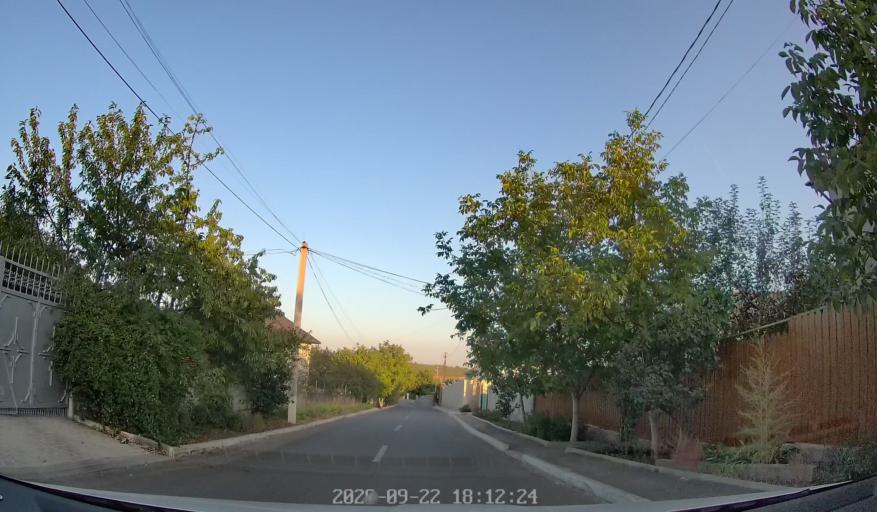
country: MD
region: Laloveni
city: Ialoveni
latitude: 46.9477
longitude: 28.7885
